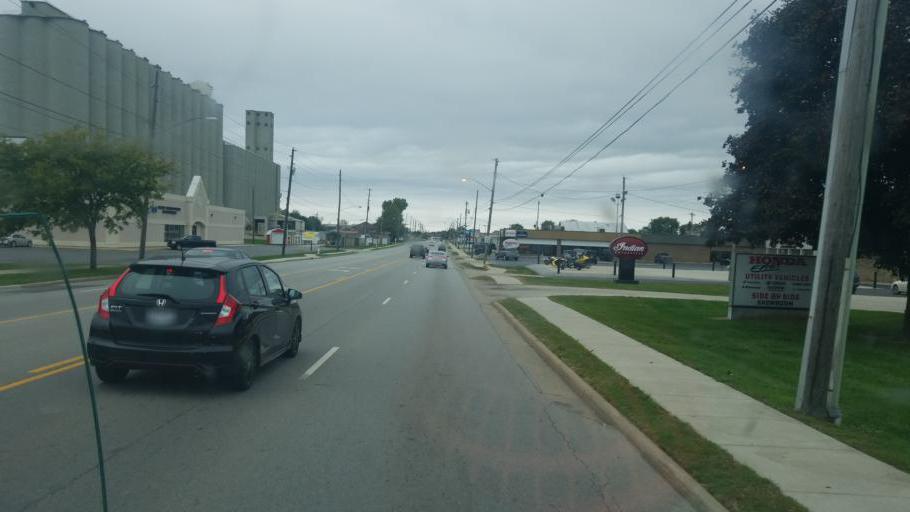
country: US
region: Ohio
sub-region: Lucas County
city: Maumee
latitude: 41.5697
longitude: -83.6575
